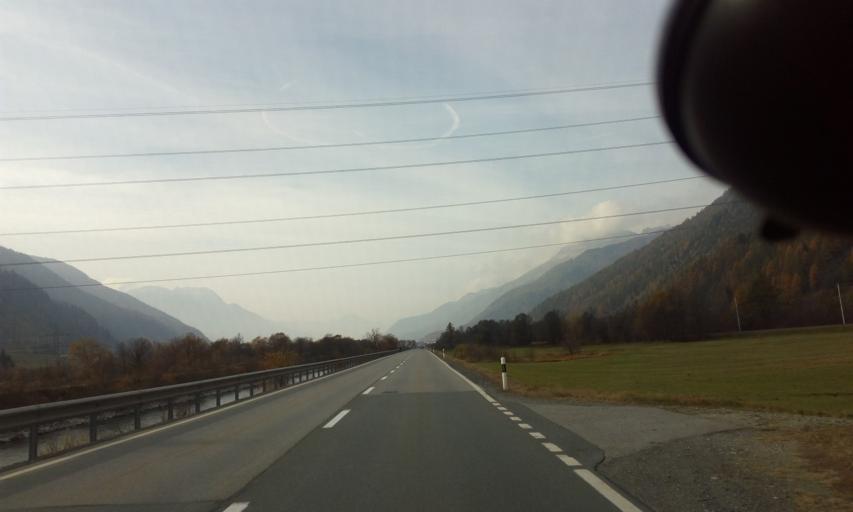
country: CH
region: Grisons
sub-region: Maloja District
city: Ponte
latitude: 46.5706
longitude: 9.9156
